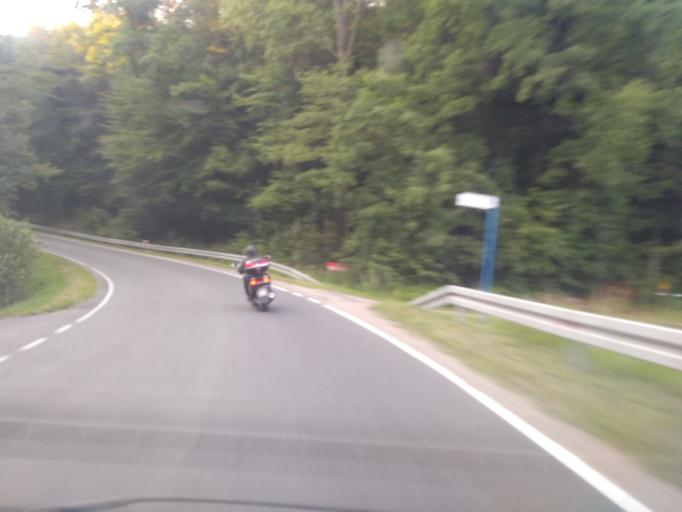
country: PL
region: Subcarpathian Voivodeship
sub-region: Powiat krosnienski
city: Korczyna
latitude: 49.7406
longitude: 21.8090
